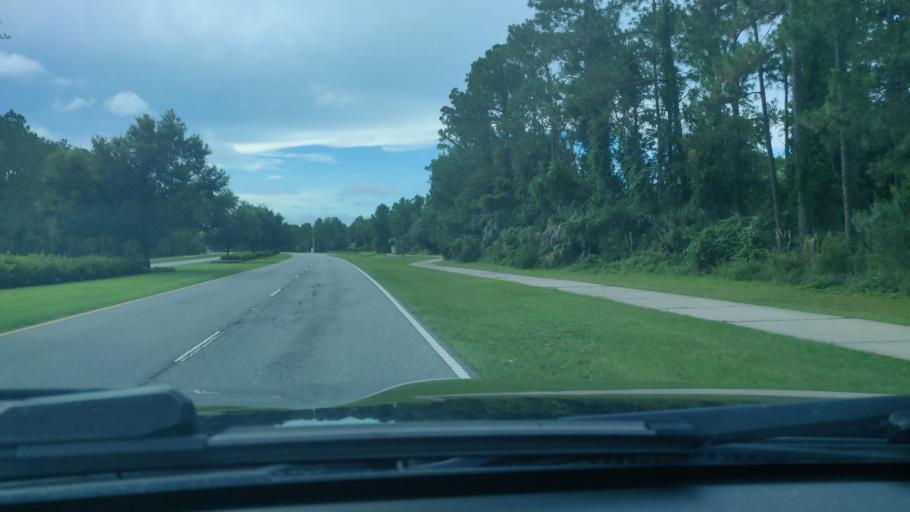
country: US
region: Florida
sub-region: Flagler County
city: Palm Coast
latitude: 29.5398
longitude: -81.2274
